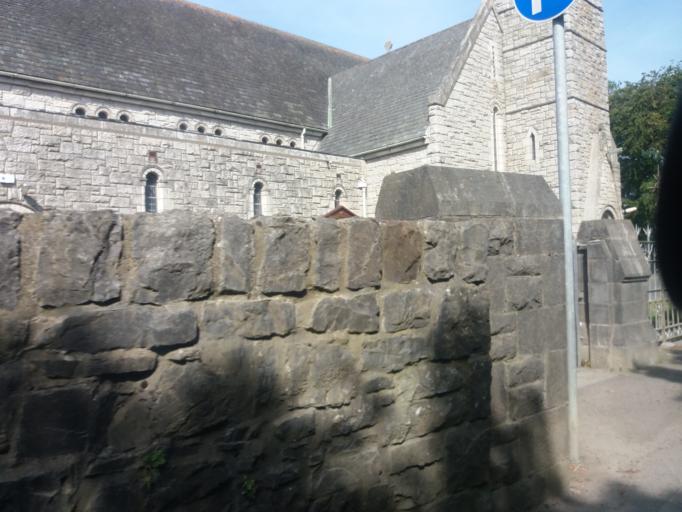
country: IE
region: Leinster
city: Lusk
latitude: 53.5297
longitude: -6.1709
